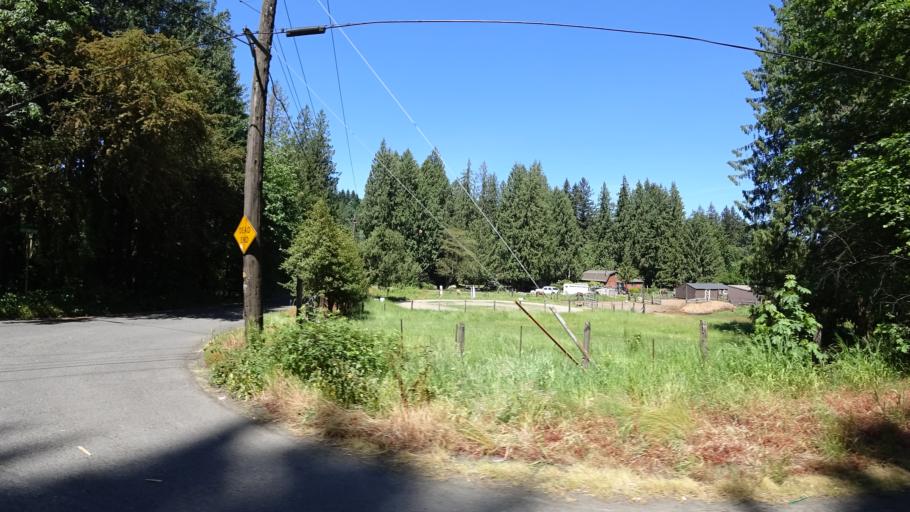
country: US
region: Oregon
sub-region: Clackamas County
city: Happy Valley
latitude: 45.4760
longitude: -122.5008
